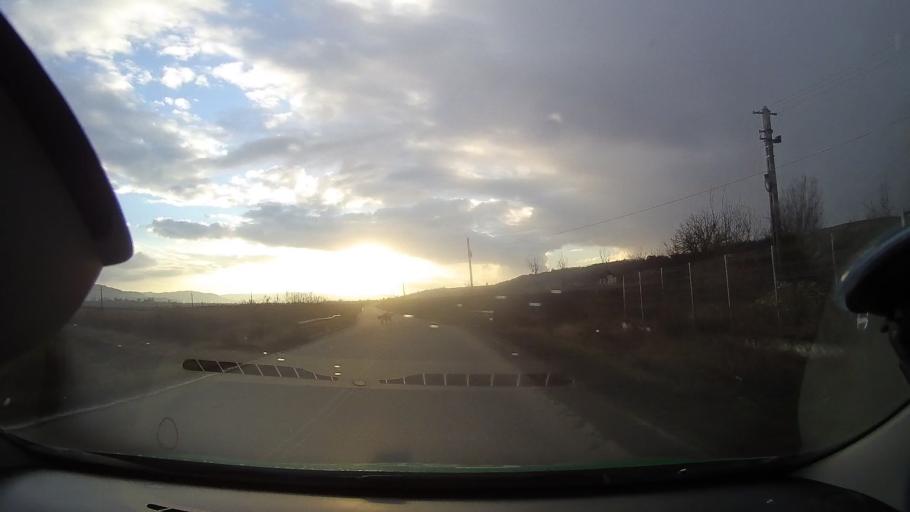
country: RO
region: Alba
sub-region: Comuna Lunca Muresului
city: Lunca Muresului
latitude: 46.4264
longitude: 23.8885
